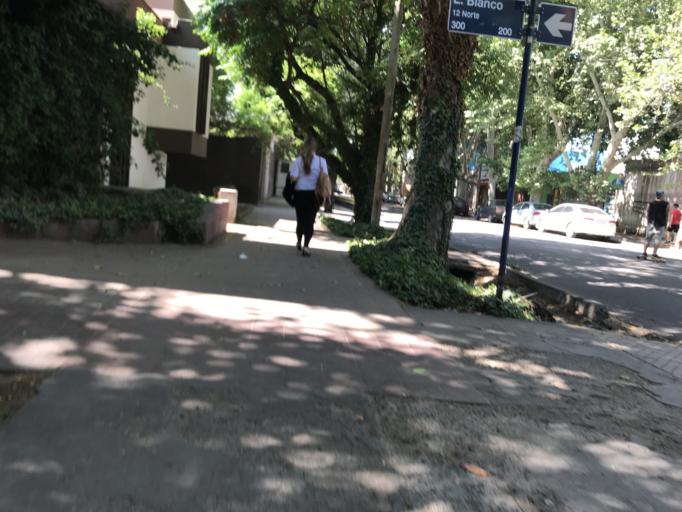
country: AR
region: Mendoza
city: Mendoza
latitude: -32.8810
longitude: -68.8396
